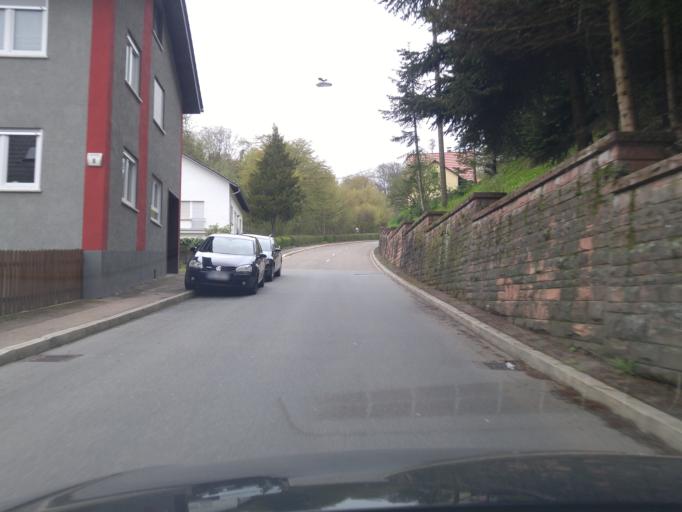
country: DE
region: Baden-Wuerttemberg
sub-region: Karlsruhe Region
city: Reichartshausen
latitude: 49.3775
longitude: 8.9615
